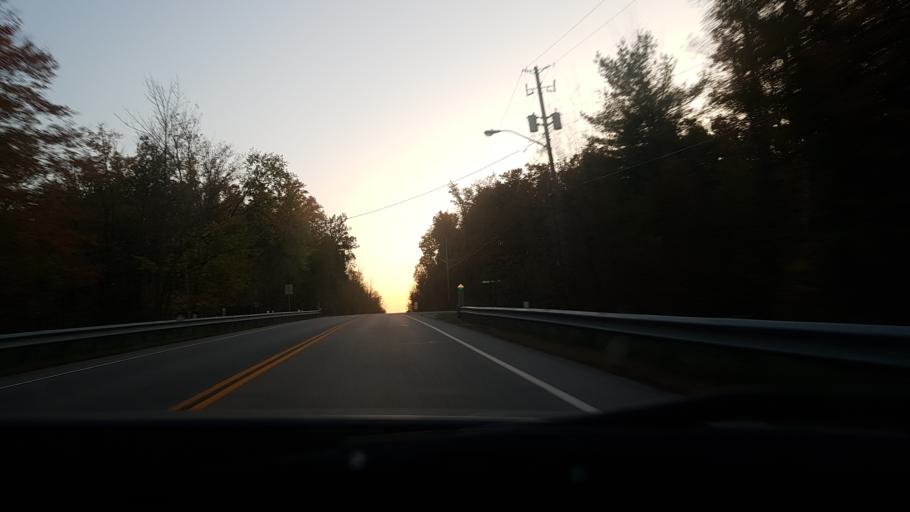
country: CA
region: Ontario
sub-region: Halton
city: Milton
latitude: 43.4641
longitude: -80.0054
